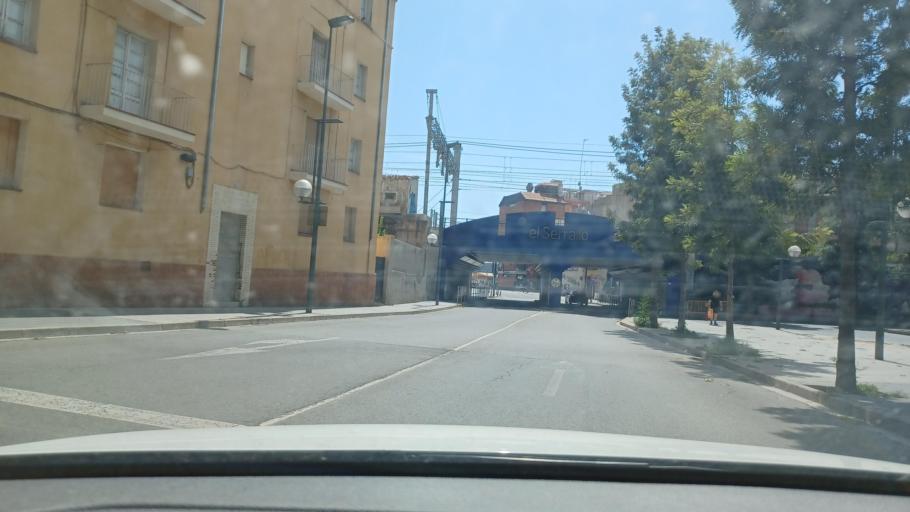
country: ES
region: Catalonia
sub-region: Provincia de Tarragona
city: Tarragona
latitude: 41.1113
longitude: 1.2426
